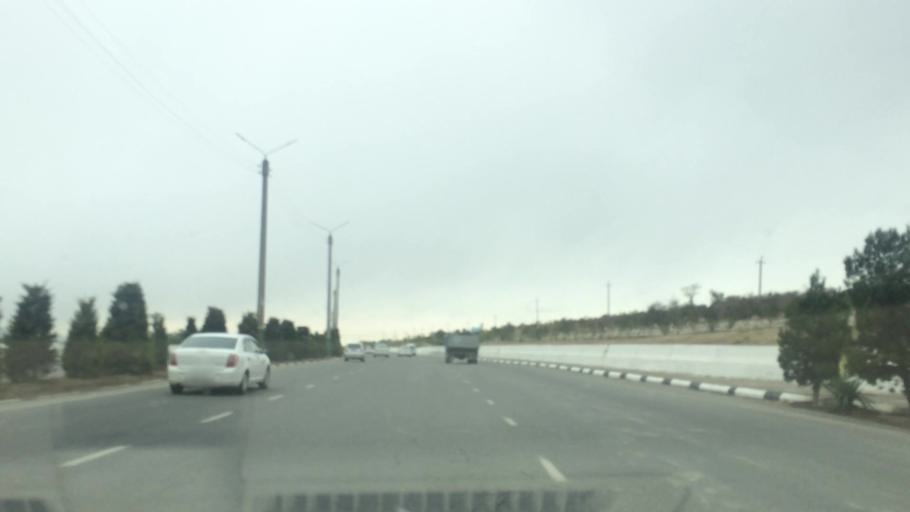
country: UZ
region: Samarqand
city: Jomboy
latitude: 39.6756
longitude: 67.0398
